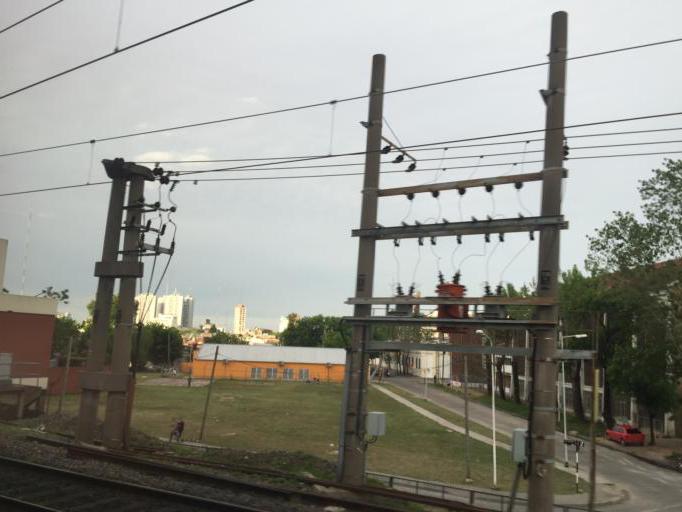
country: AR
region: Buenos Aires
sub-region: Partido de Avellaneda
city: Avellaneda
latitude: -34.6653
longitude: -58.3758
